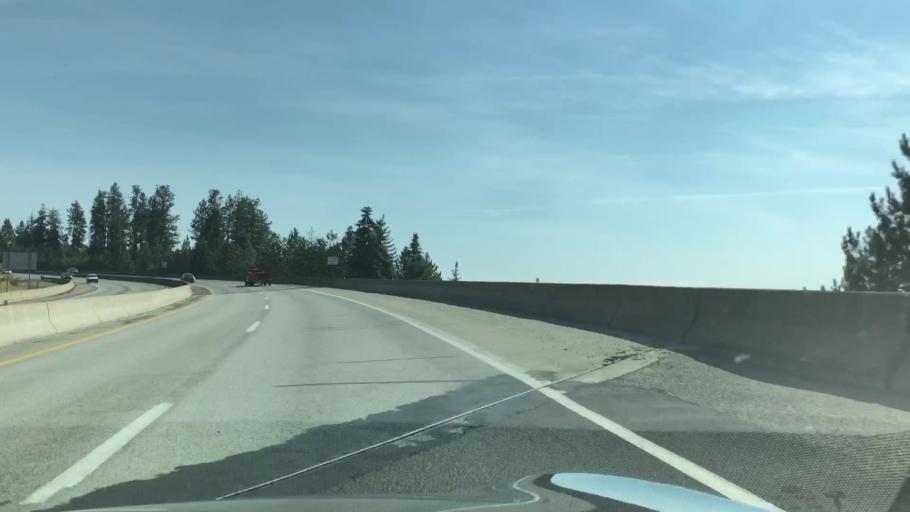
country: US
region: Idaho
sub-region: Kootenai County
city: Coeur d'Alene
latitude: 47.6660
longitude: -116.7507
